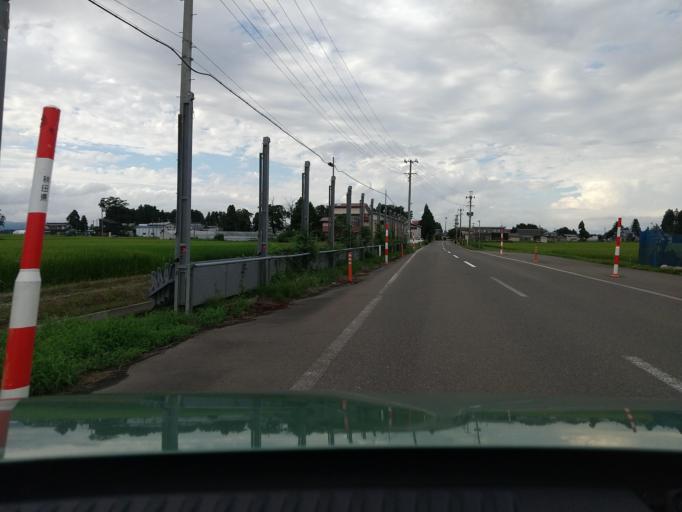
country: JP
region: Akita
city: Yokotemachi
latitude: 39.2880
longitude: 140.4810
